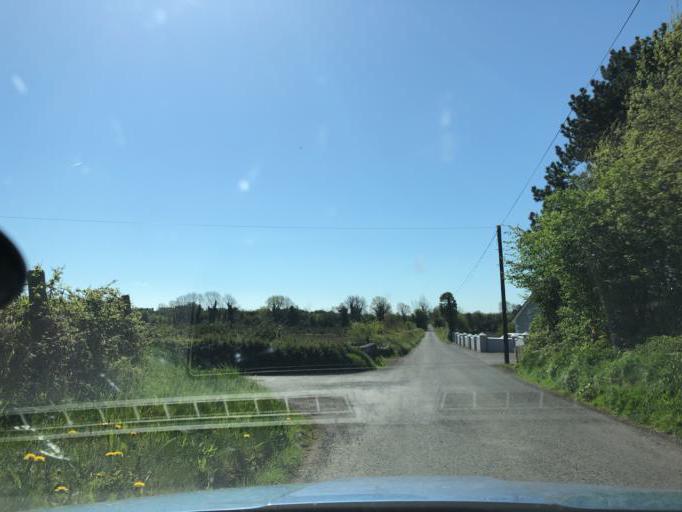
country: IE
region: Connaught
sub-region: County Galway
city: Portumna
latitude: 53.1374
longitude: -8.3361
